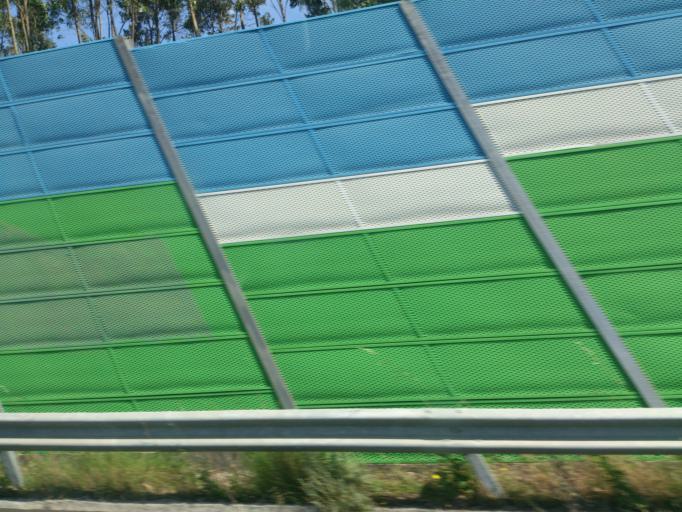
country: PT
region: Lisbon
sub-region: Mafra
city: Malveira
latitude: 38.9361
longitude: -9.2909
